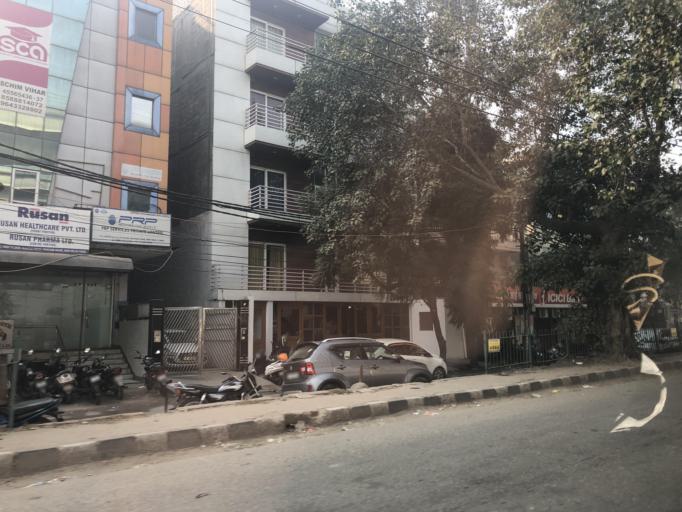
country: IN
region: NCT
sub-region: West Delhi
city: Nangloi Jat
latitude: 28.6790
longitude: 77.0977
